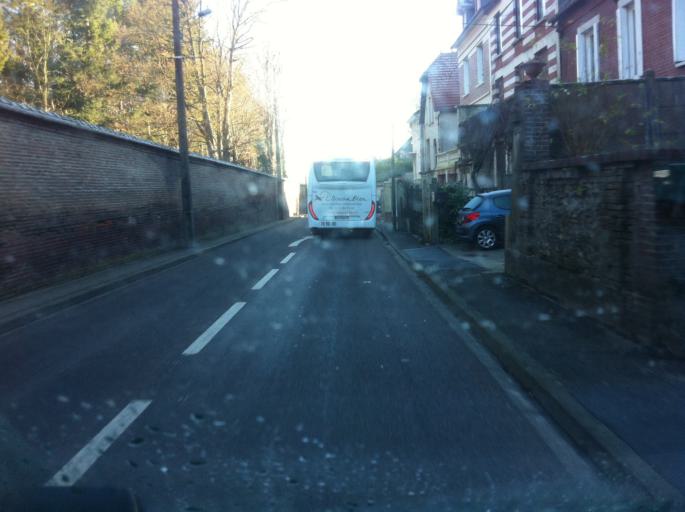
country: FR
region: Haute-Normandie
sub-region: Departement de la Seine-Maritime
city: Eu
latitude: 50.0487
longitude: 1.4115
